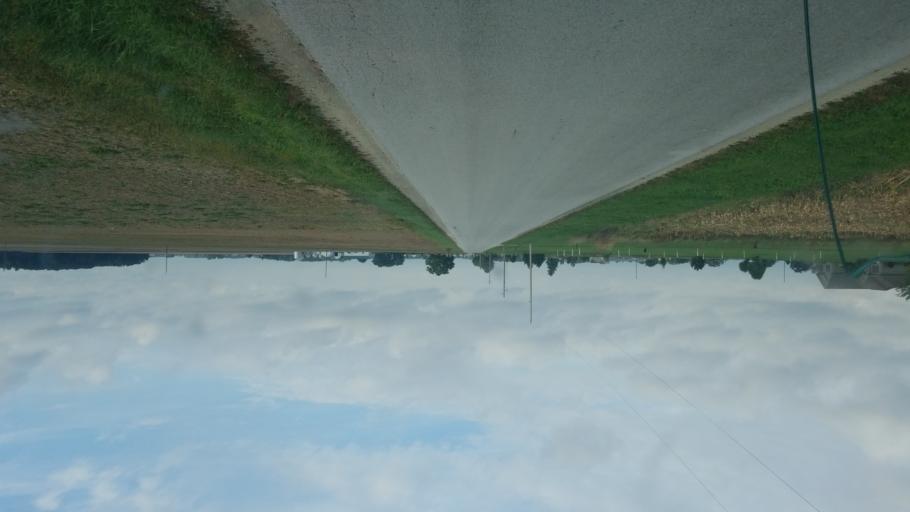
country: US
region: Ohio
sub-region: Wyandot County
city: Carey
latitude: 40.9769
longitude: -83.4295
